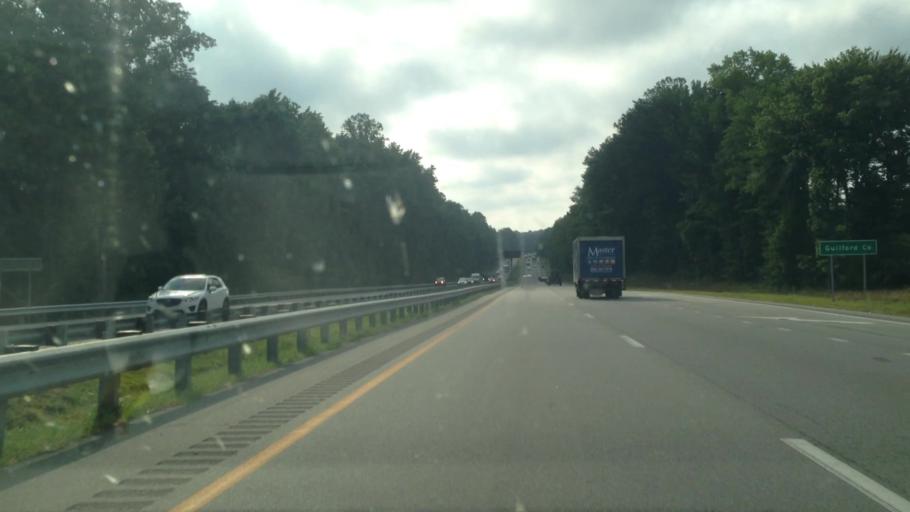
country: US
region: North Carolina
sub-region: Forsyth County
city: Kernersville
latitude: 36.1053
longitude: -80.0400
